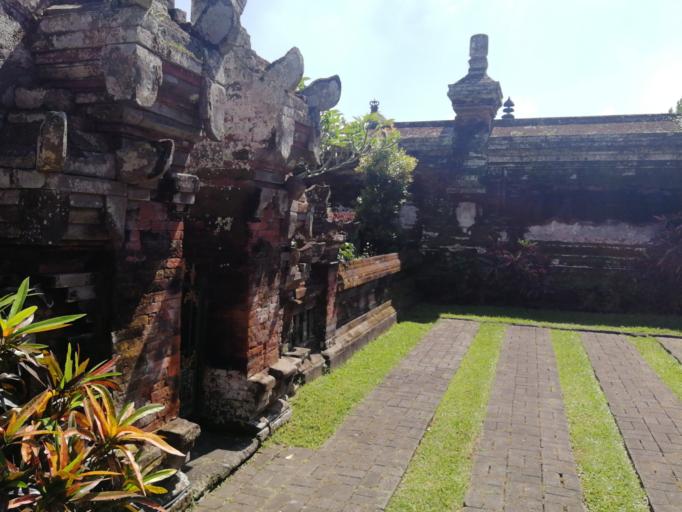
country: ID
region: Bali
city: Banjar Serangan
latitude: -8.5424
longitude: 115.1725
